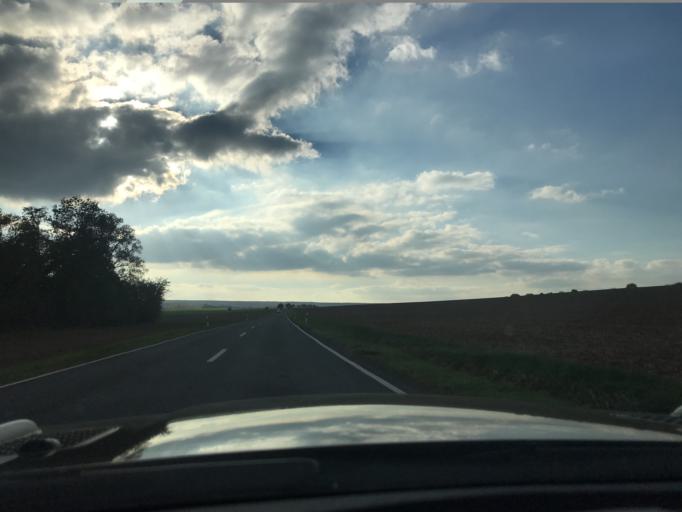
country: DE
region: Thuringia
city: Schonstedt
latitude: 51.1156
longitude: 10.5419
